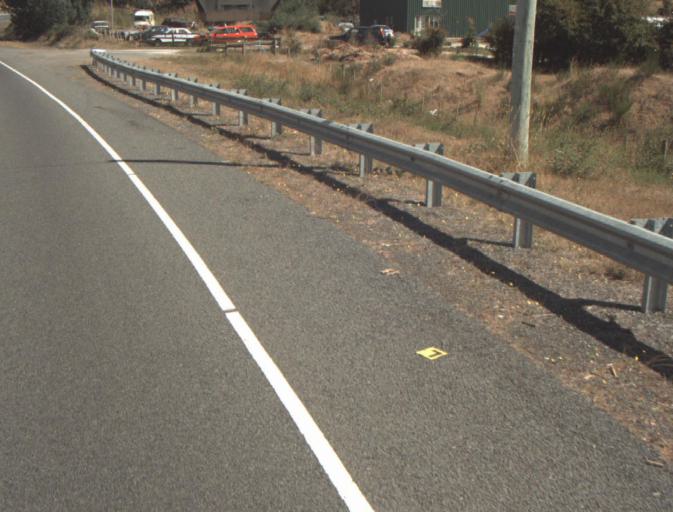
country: AU
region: Tasmania
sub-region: Launceston
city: Newstead
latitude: -41.4256
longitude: 147.1854
